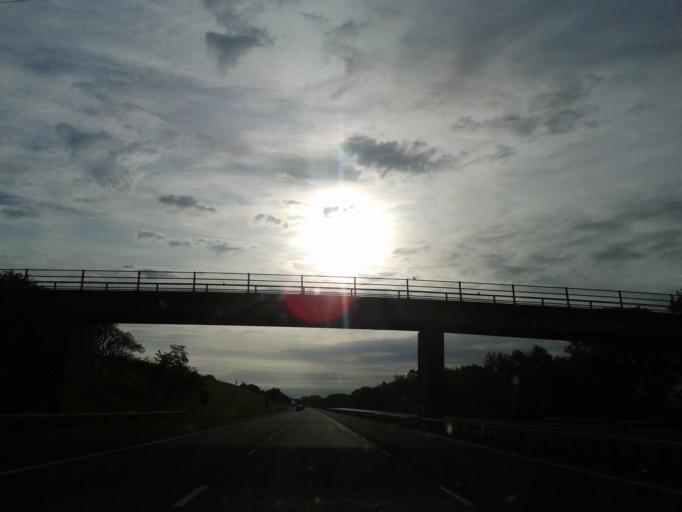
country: GB
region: Scotland
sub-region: Dumfries and Galloway
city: Gretna
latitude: 55.0130
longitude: -3.1000
